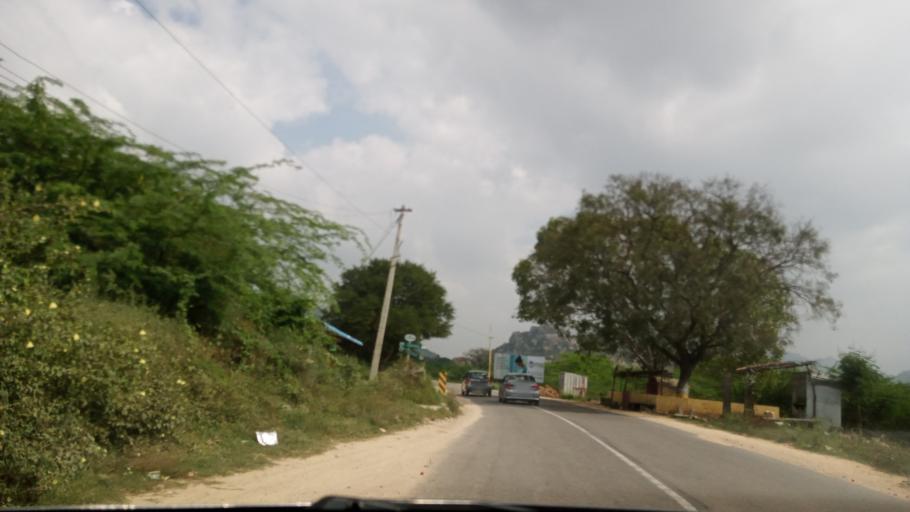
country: IN
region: Andhra Pradesh
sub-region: Chittoor
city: Madanapalle
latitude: 13.6422
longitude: 78.5581
